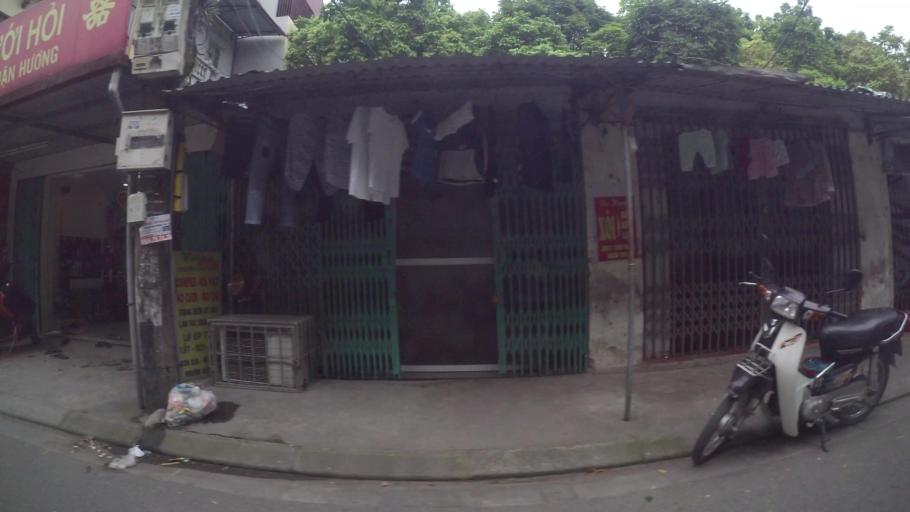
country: VN
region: Ha Noi
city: Hoan Kiem
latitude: 21.0651
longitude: 105.8834
